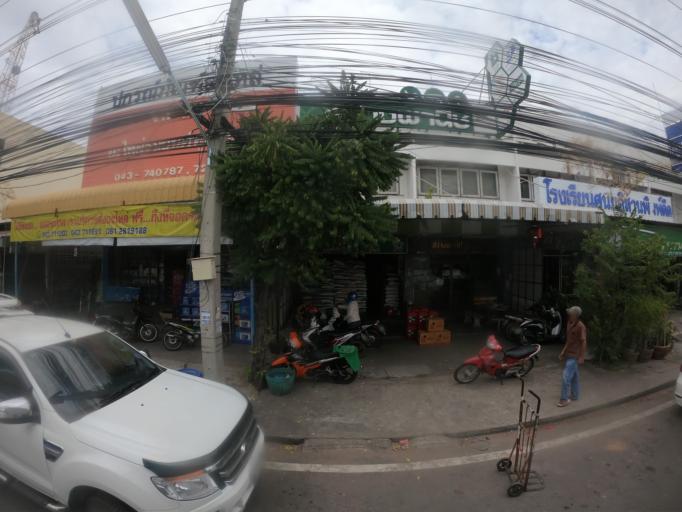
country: TH
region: Maha Sarakham
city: Maha Sarakham
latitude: 16.1803
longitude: 103.3043
